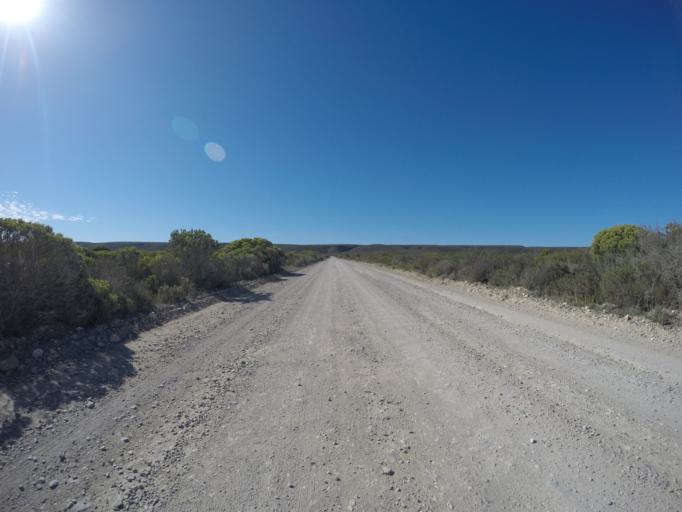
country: ZA
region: Western Cape
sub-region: Overberg District Municipality
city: Bredasdorp
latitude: -34.4397
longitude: 20.4209
